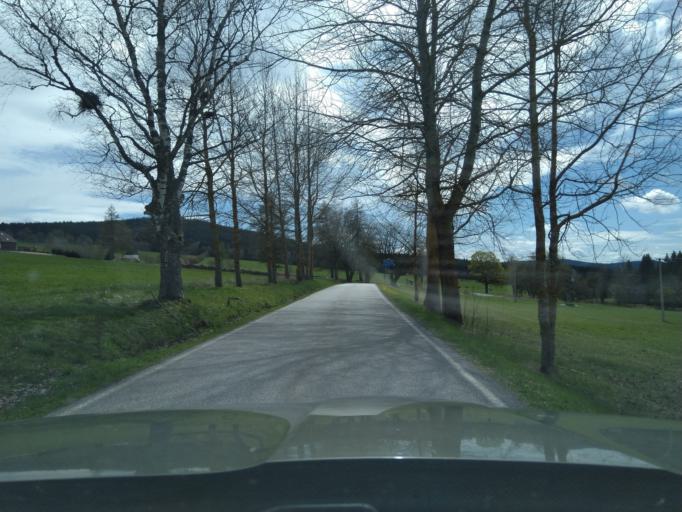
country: CZ
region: Jihocesky
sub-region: Okres Prachatice
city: Borova Lada
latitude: 49.0276
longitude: 13.6663
